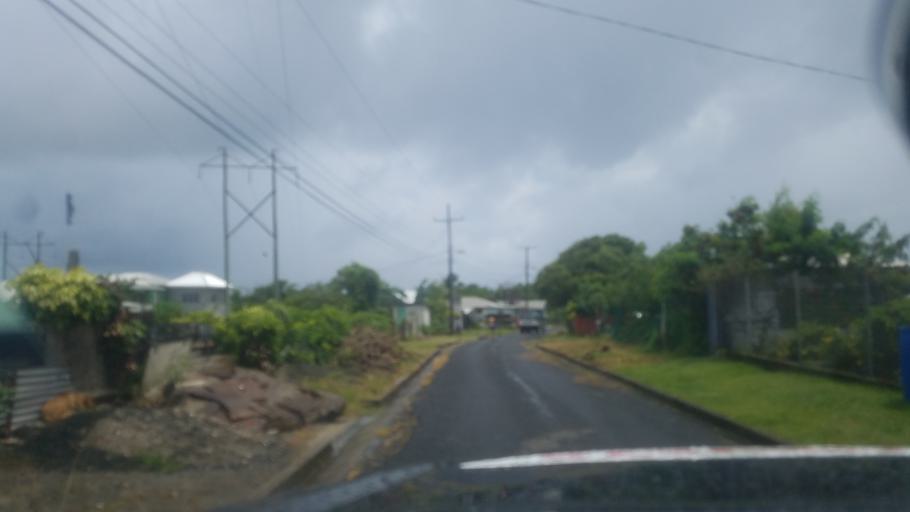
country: LC
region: Laborie Quarter
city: Laborie
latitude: 13.7544
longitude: -60.9773
